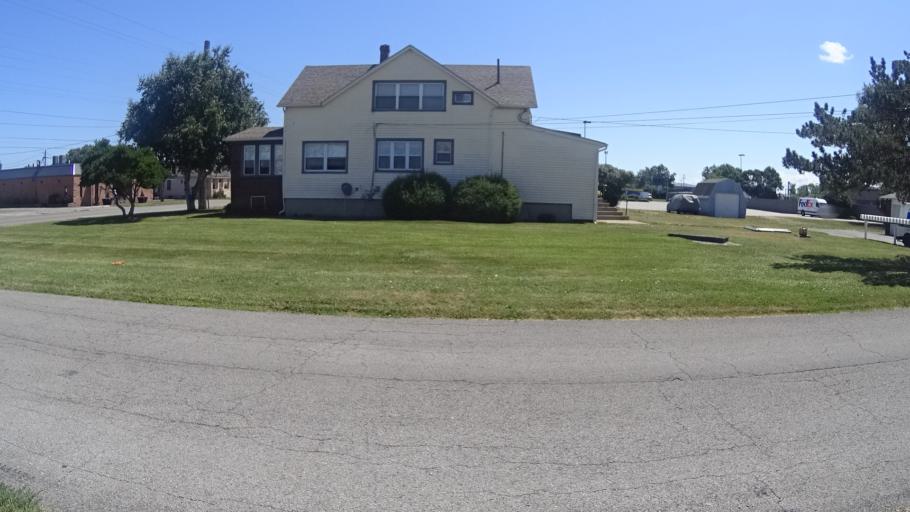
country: US
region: Ohio
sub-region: Erie County
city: Sandusky
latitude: 41.4328
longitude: -82.7088
